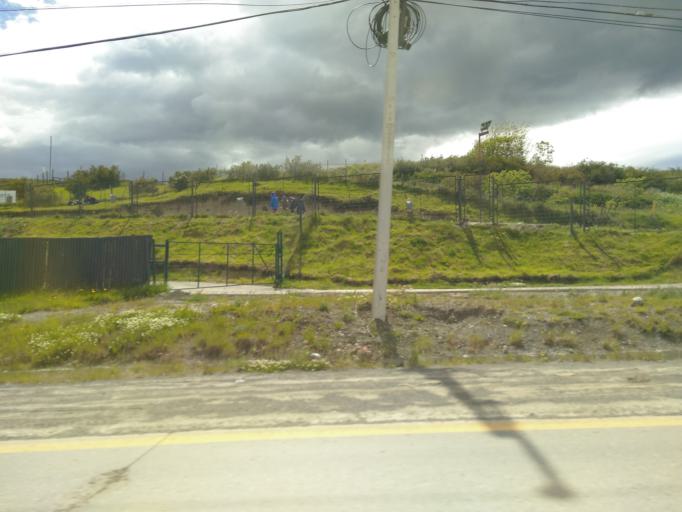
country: CL
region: Magallanes
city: Puerto Natales
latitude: -51.6998
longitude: -72.5202
